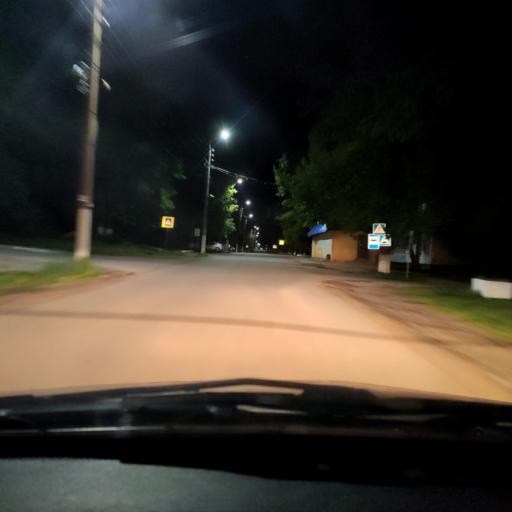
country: RU
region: Bashkortostan
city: Avdon
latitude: 54.6568
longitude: 55.5967
